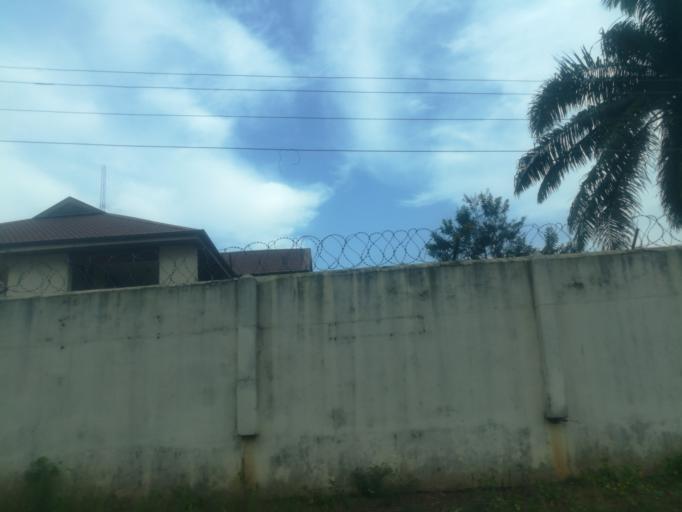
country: NG
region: Oyo
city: Ibadan
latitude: 7.4177
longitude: 3.9055
